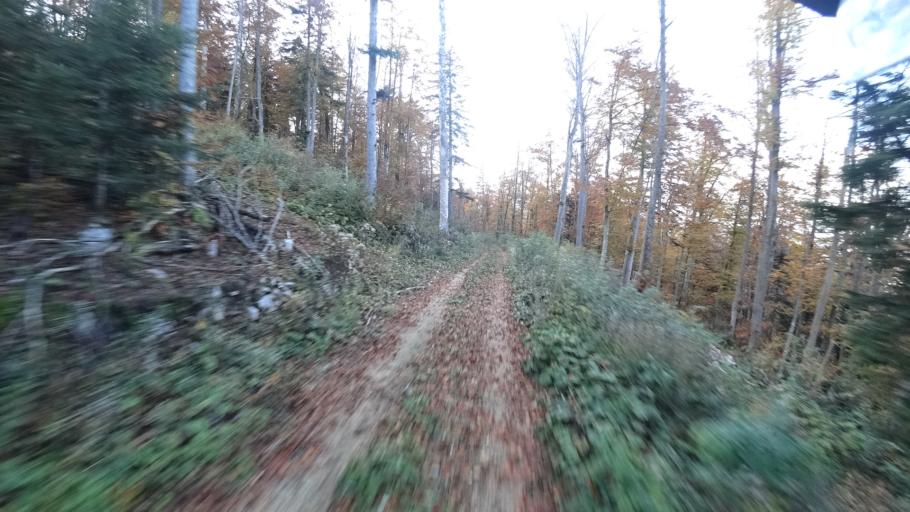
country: HR
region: Karlovacka
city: Plaski
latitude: 44.9580
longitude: 15.4047
